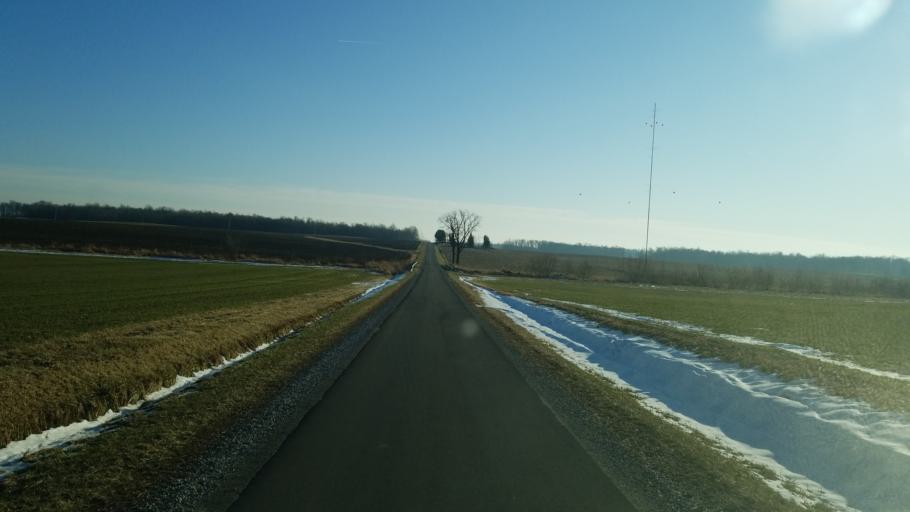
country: US
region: Ohio
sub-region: Crawford County
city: Bucyrus
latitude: 40.9924
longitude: -82.9587
